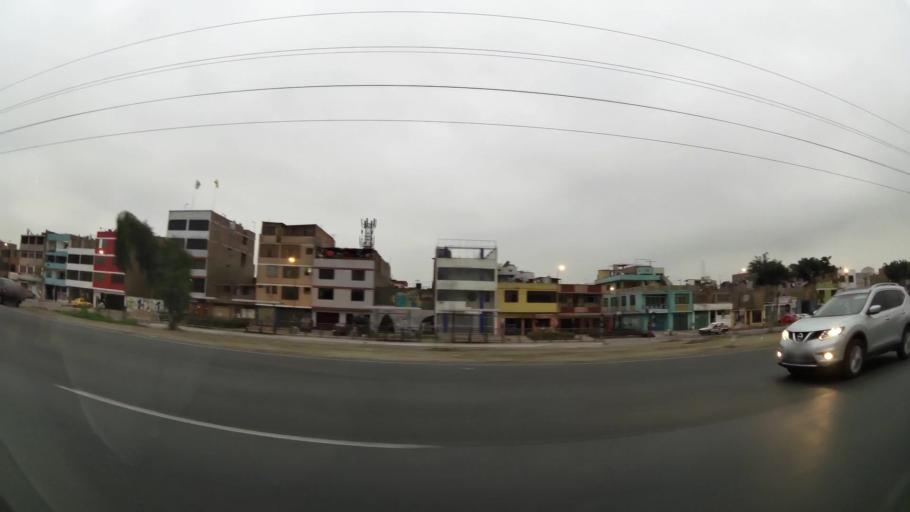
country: PE
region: Lima
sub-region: Lima
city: Independencia
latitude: -11.9728
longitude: -77.0666
